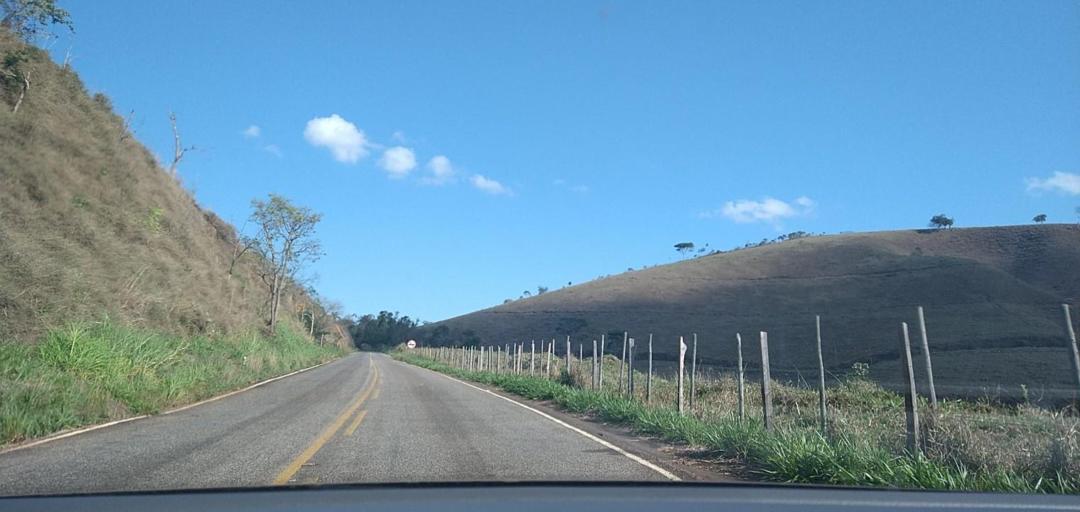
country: BR
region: Minas Gerais
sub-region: Alvinopolis
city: Alvinopolis
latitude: -20.1914
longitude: -42.9382
